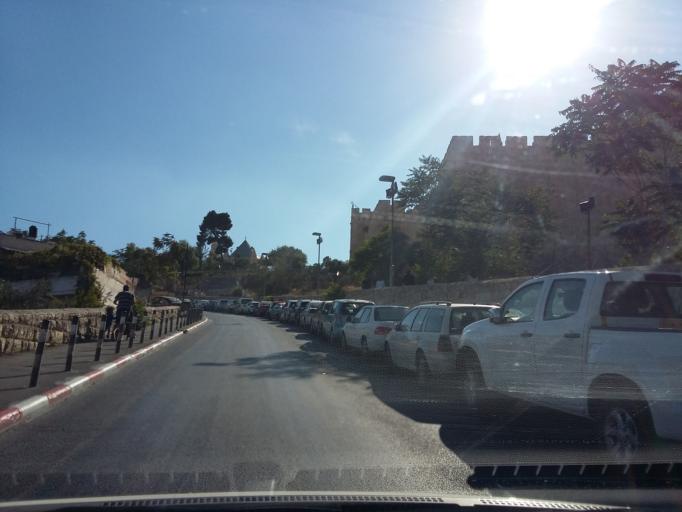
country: PS
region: West Bank
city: Old City
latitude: 31.7732
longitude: 35.2323
